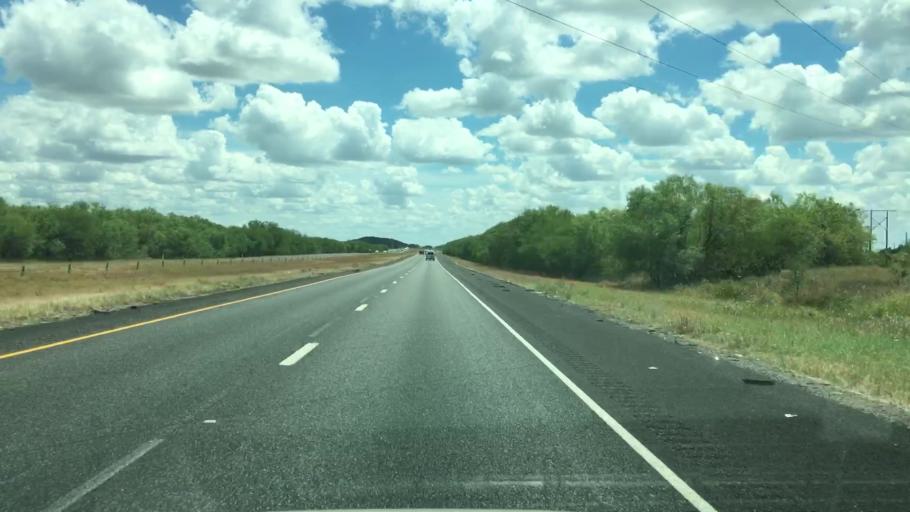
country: US
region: Texas
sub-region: Atascosa County
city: Pleasanton
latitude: 28.7453
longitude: -98.2934
